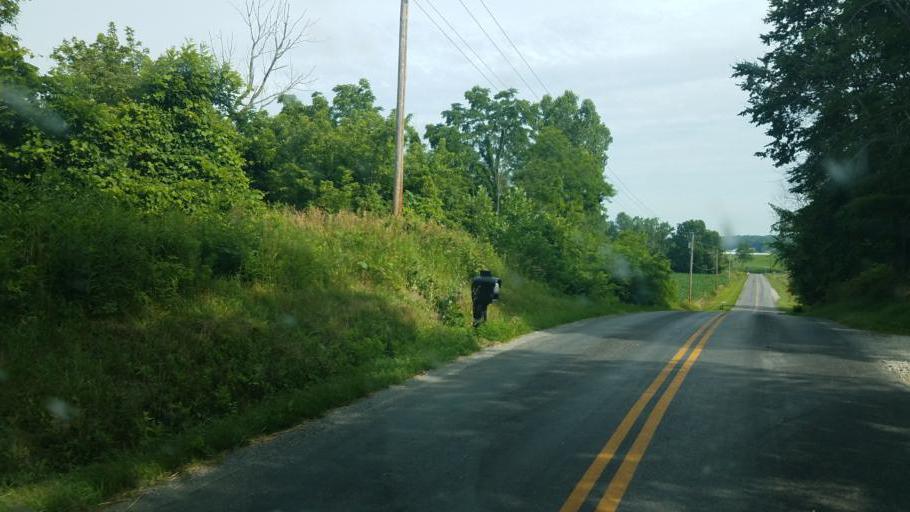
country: US
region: Ohio
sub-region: Medina County
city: Lodi
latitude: 41.0472
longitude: -82.0344
